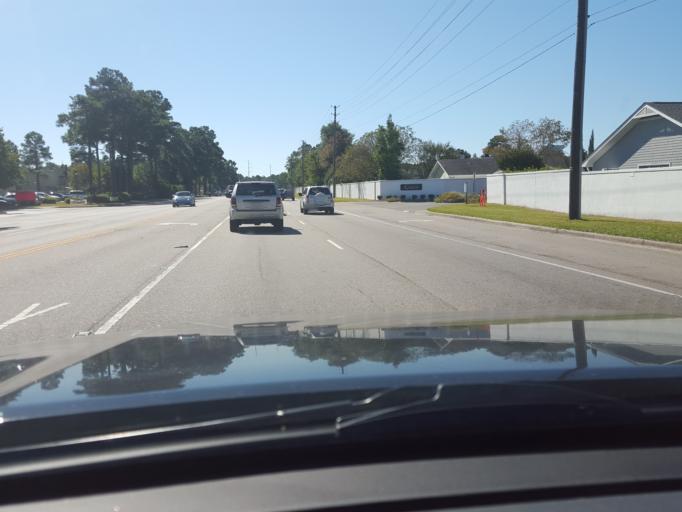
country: US
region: North Carolina
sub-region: New Hanover County
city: Seagate
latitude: 34.2307
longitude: -77.8293
